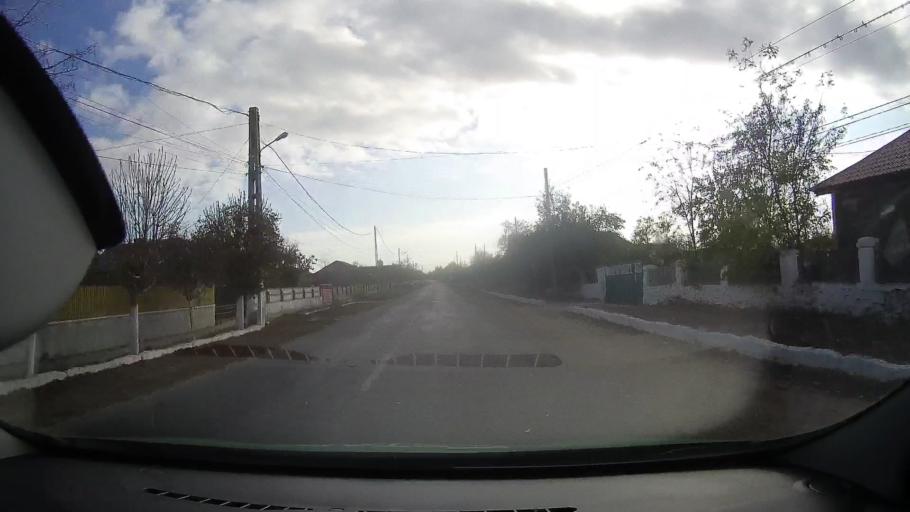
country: RO
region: Constanta
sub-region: Comuna Corbu
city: Corbu
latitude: 44.4186
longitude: 28.6609
